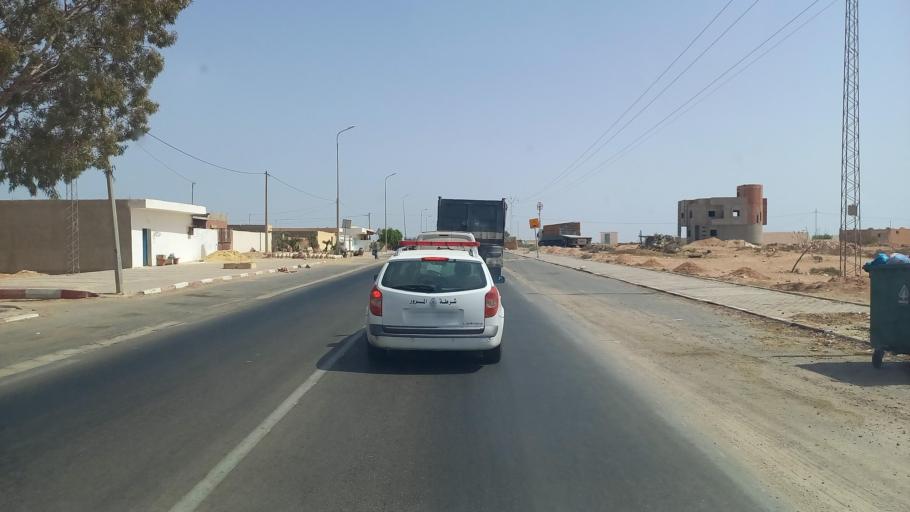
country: TN
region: Madanin
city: Medenine
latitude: 33.3740
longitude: 10.6934
